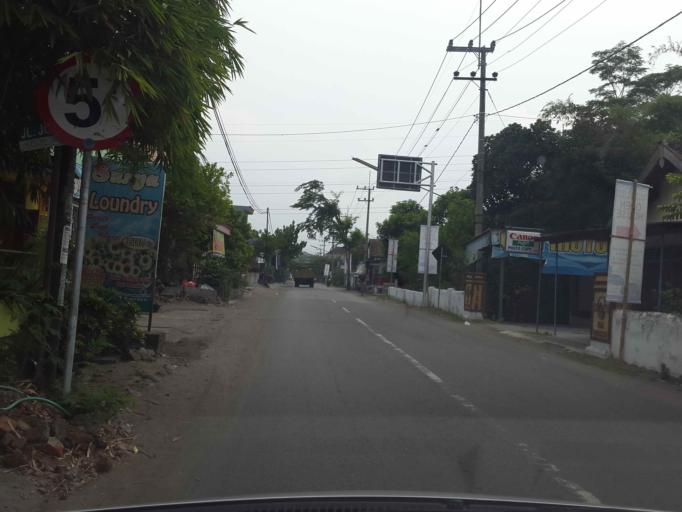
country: ID
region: East Java
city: Kediri
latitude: -7.7945
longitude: 112.0378
